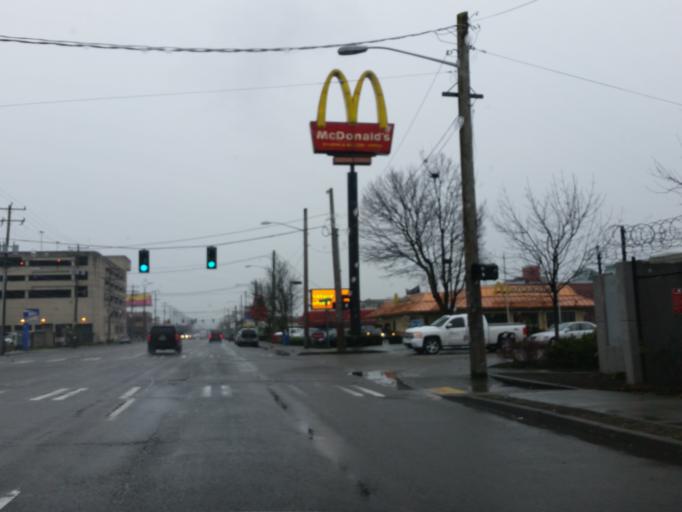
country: US
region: Washington
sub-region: King County
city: Seattle
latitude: 47.5823
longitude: -122.3292
